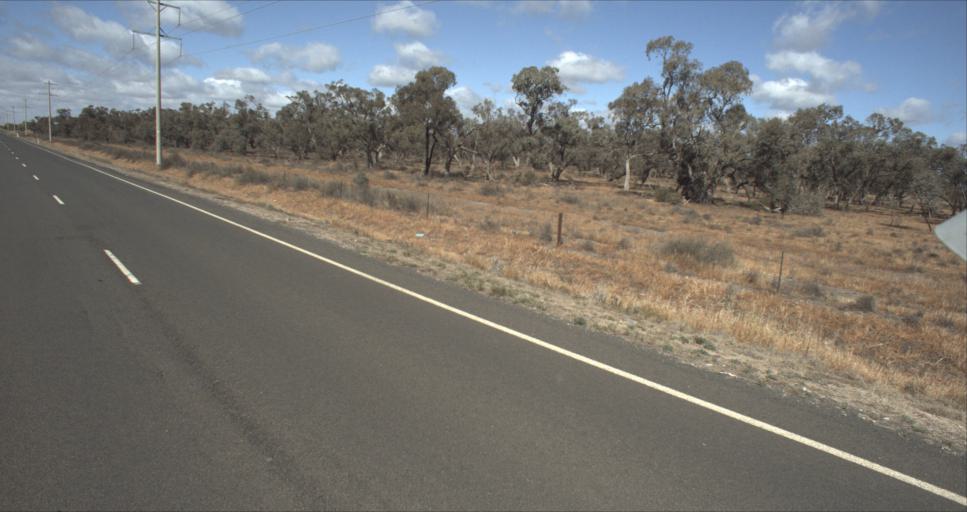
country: AU
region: New South Wales
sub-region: Murrumbidgee Shire
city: Darlington Point
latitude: -34.5213
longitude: 146.1757
